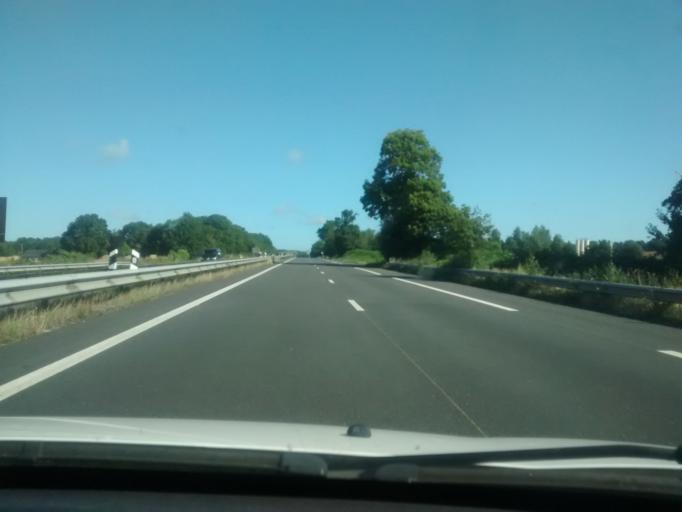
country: FR
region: Brittany
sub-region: Departement d'Ille-et-Vilaine
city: Saint-Pierre-de-Plesguen
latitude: 48.4221
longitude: -1.9110
